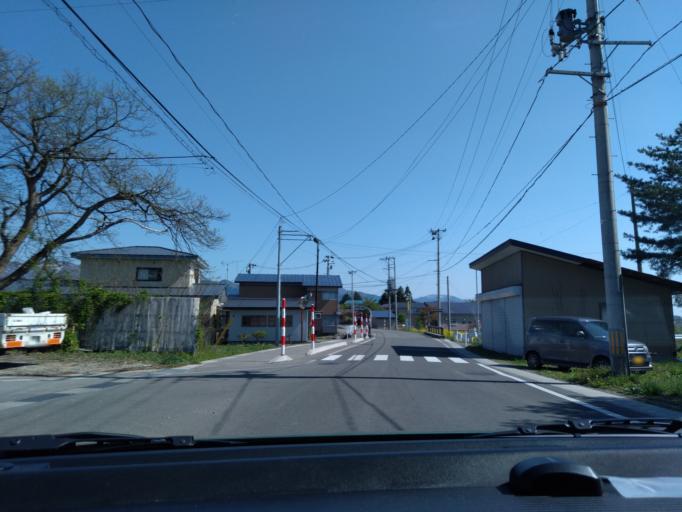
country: JP
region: Akita
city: Kakunodatemachi
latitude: 39.5108
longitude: 140.5935
